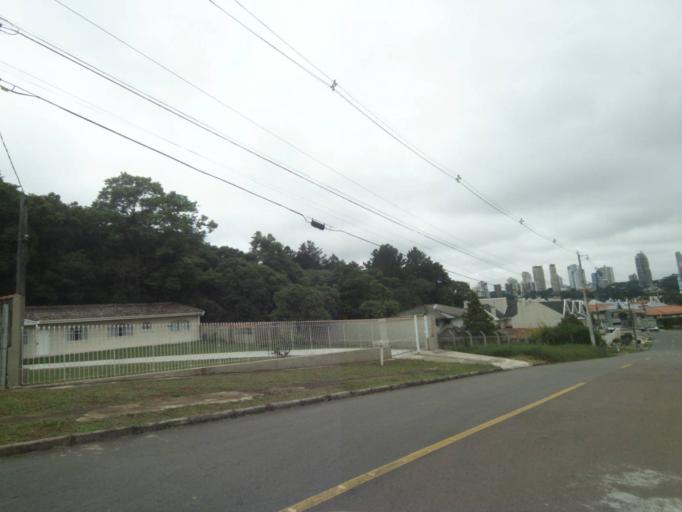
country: BR
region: Parana
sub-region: Curitiba
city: Curitiba
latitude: -25.4259
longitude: -49.3364
